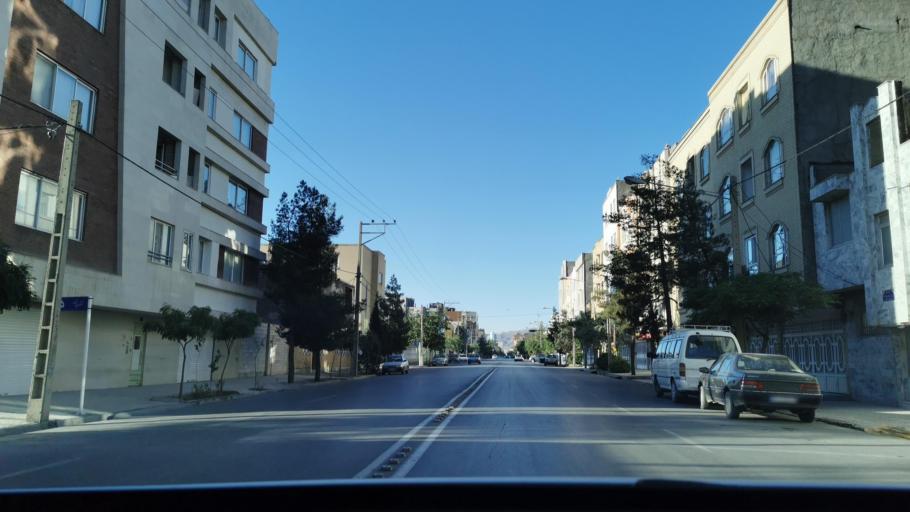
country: IR
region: Razavi Khorasan
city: Mashhad
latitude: 36.3563
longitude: 59.4972
